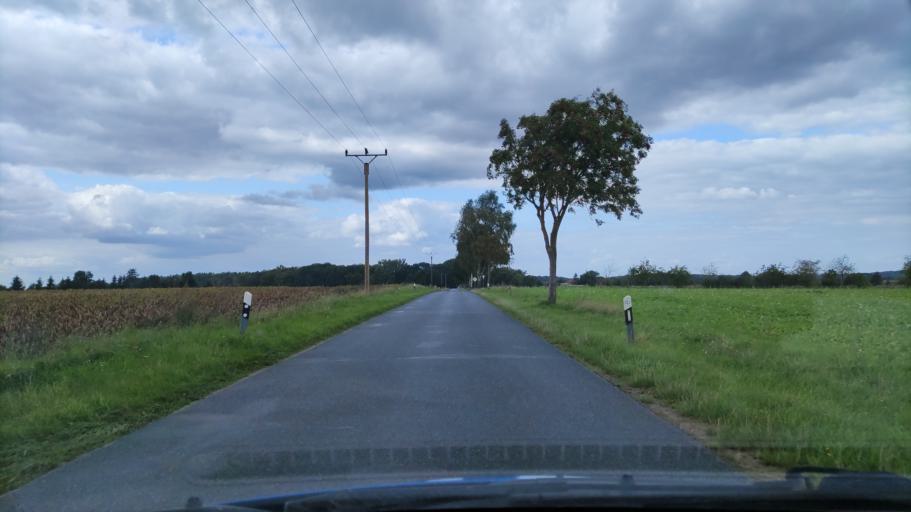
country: DE
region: Lower Saxony
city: Weste
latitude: 53.0543
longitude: 10.7124
